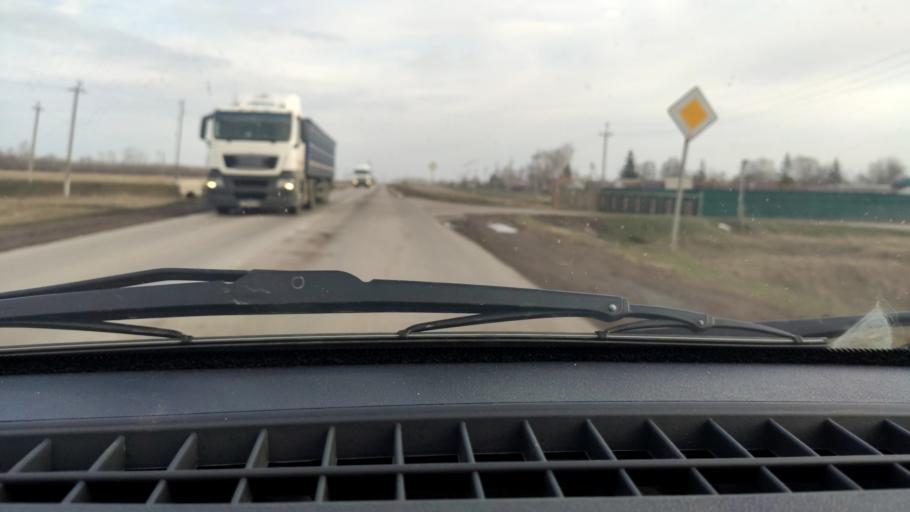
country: RU
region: Bashkortostan
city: Davlekanovo
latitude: 54.3769
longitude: 55.1956
